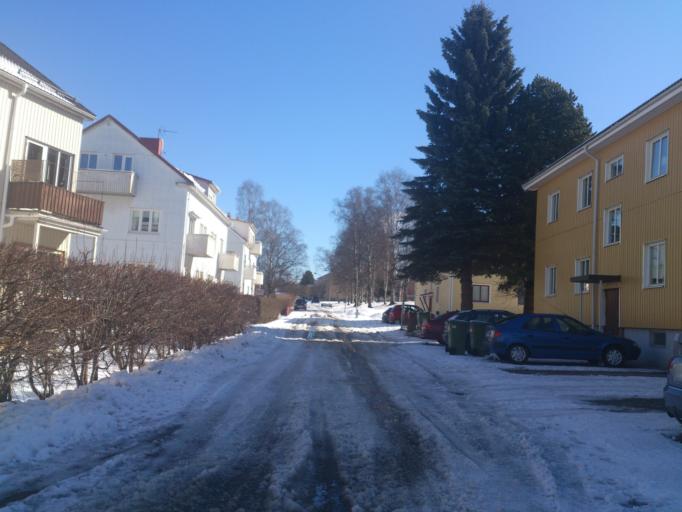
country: SE
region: Vaesternorrland
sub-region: Sundsvalls Kommun
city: Sundsvall
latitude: 62.3806
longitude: 17.3222
